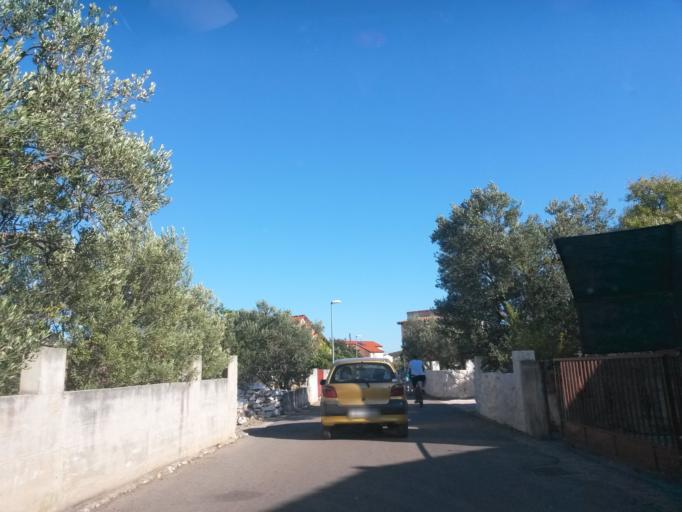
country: HR
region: Sibensko-Kniniska
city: Rogoznica
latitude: 43.5388
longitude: 15.9611
